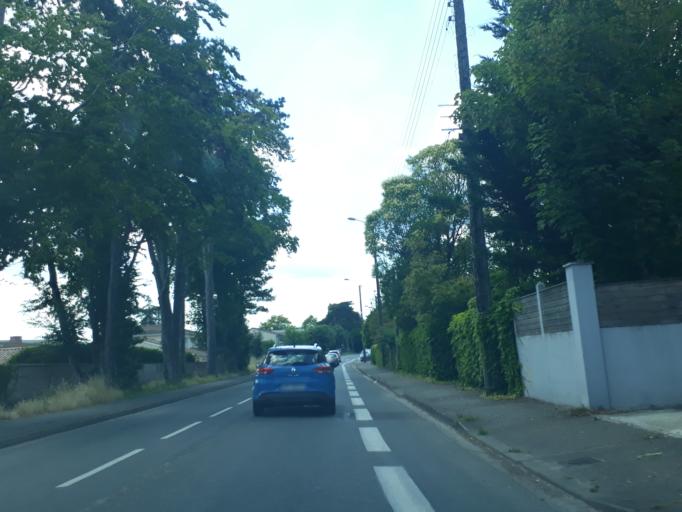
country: FR
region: Aquitaine
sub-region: Departement de la Gironde
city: Merignac
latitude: 44.8394
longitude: -0.6364
